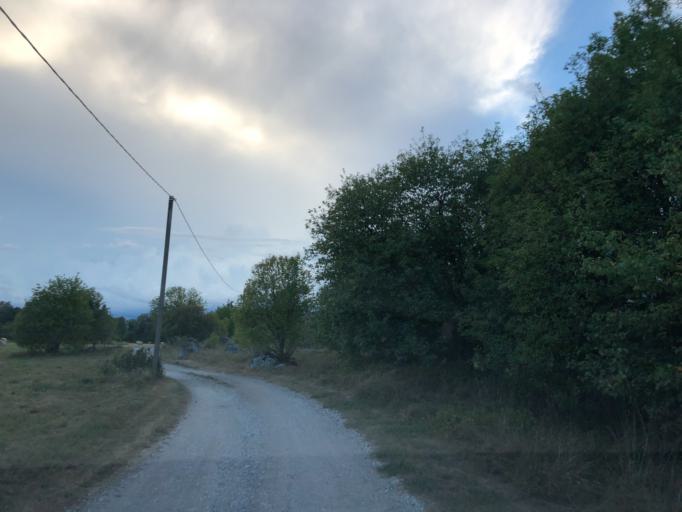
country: EE
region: Laeaene
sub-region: Haapsalu linn
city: Haapsalu
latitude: 58.7817
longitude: 23.4809
